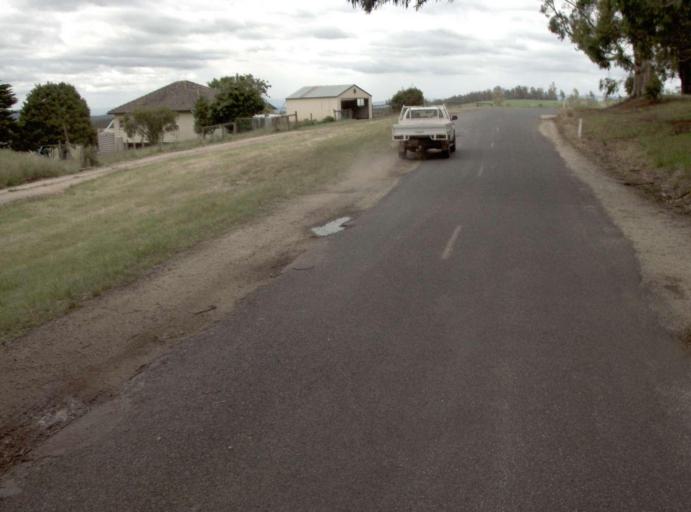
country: AU
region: Victoria
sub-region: Latrobe
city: Moe
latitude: -37.9953
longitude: 146.1466
